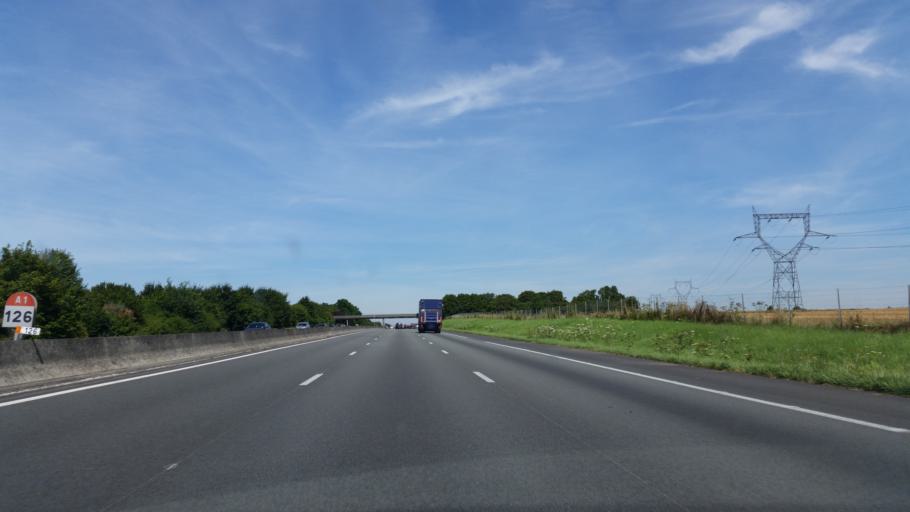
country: FR
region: Picardie
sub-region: Departement de la Somme
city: Peronne
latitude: 49.9177
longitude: 2.8511
